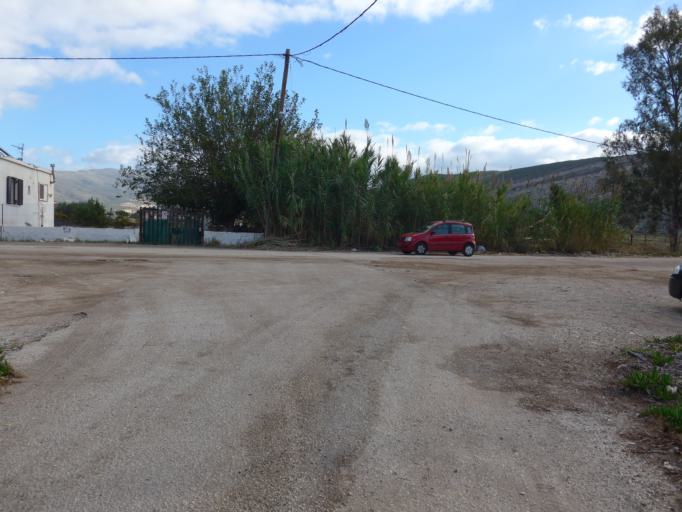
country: GR
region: Peloponnese
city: Asklipieio
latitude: 37.4778
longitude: 22.9997
